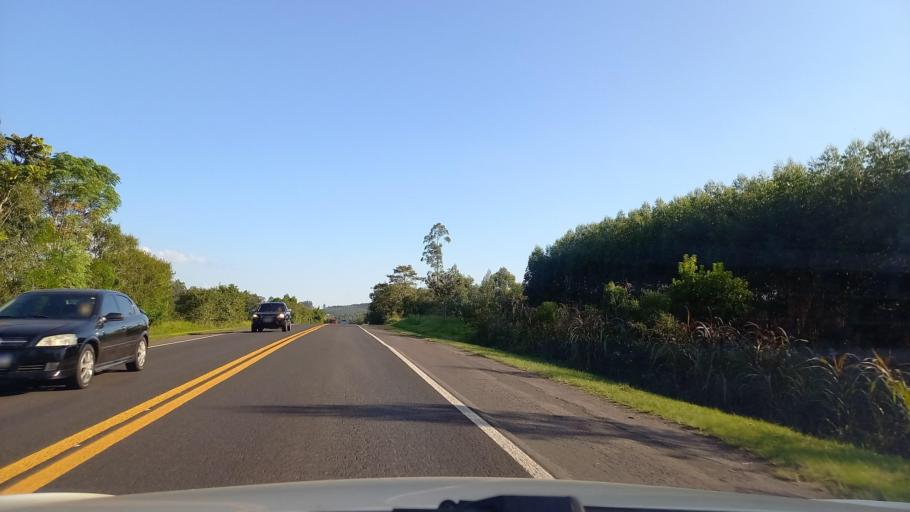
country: BR
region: Rio Grande do Sul
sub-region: Taquari
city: Taquari
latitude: -29.6942
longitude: -51.7474
